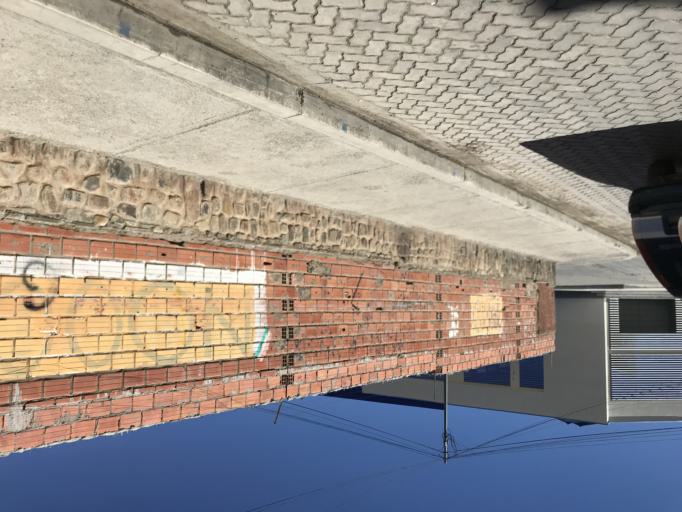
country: BO
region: La Paz
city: La Paz
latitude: -16.4882
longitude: -68.1952
